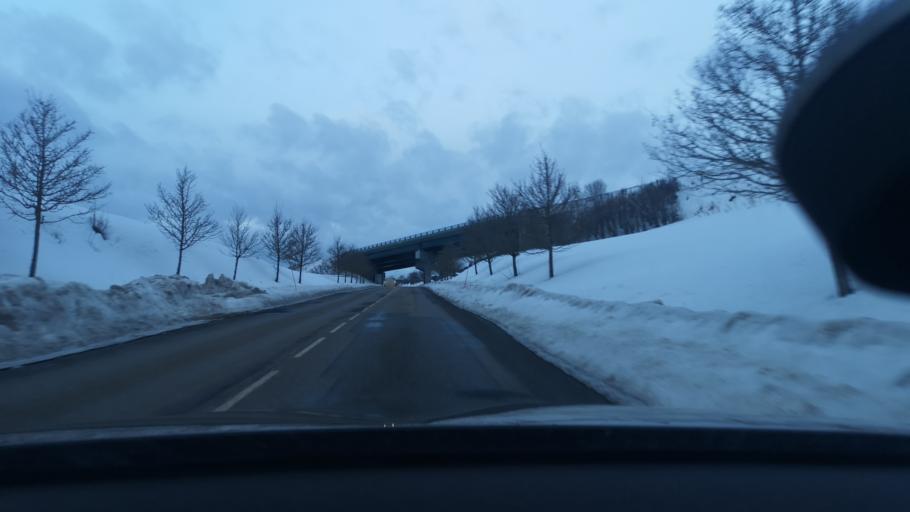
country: FR
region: Franche-Comte
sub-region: Departement du Doubs
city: Jougne
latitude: 46.7808
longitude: 6.3727
